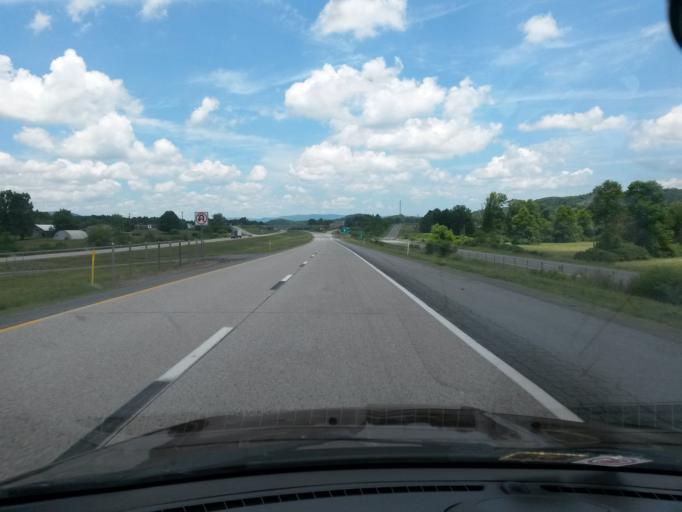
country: US
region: West Virginia
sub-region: Greenbrier County
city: Rainelle
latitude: 37.8477
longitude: -80.7271
